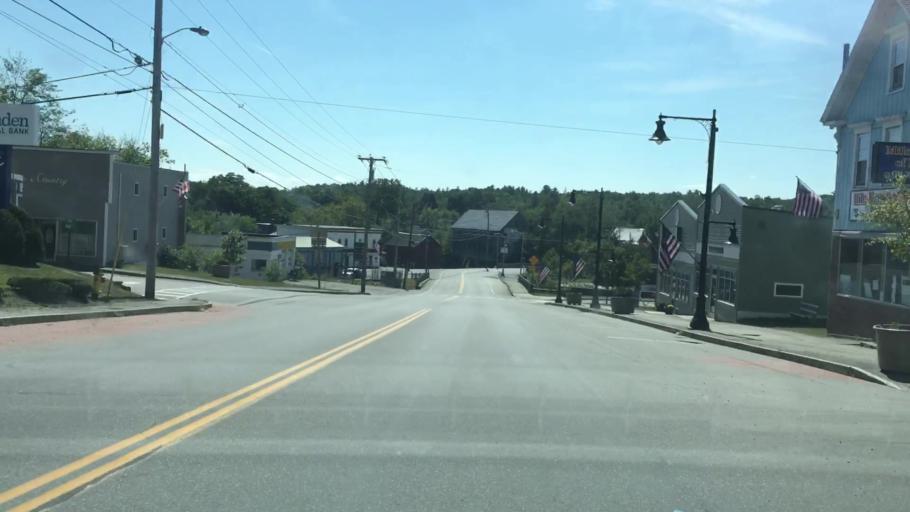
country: US
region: Maine
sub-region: Piscataquis County
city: Milo
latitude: 45.2526
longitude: -68.9865
